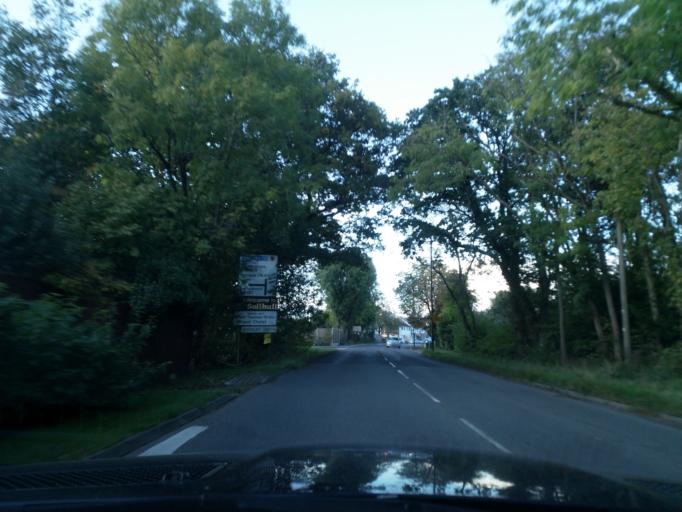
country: GB
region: England
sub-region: Solihull
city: Cheswick Green
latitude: 52.3483
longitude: -1.7772
